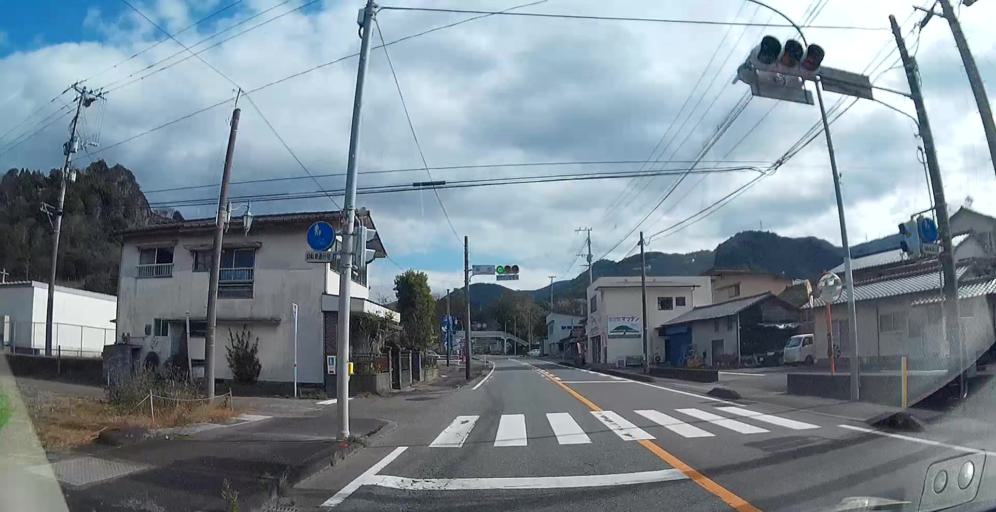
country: JP
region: Kumamoto
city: Minamata
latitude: 32.2320
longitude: 130.4549
